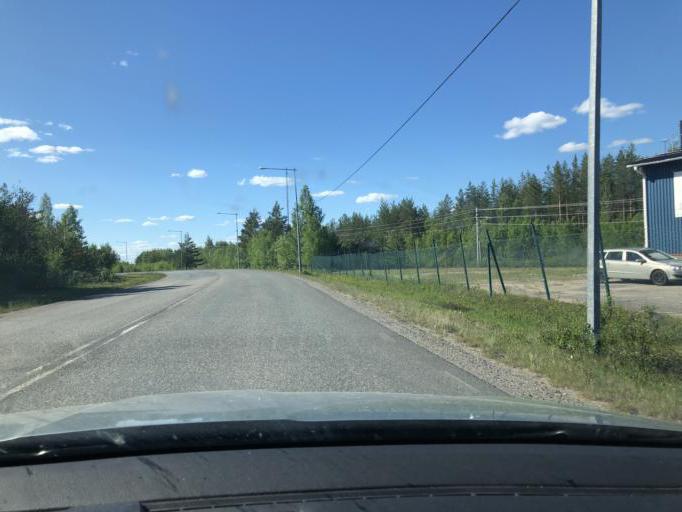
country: SE
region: Norrbotten
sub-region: Kalix Kommun
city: Kalix
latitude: 65.8607
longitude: 23.1574
